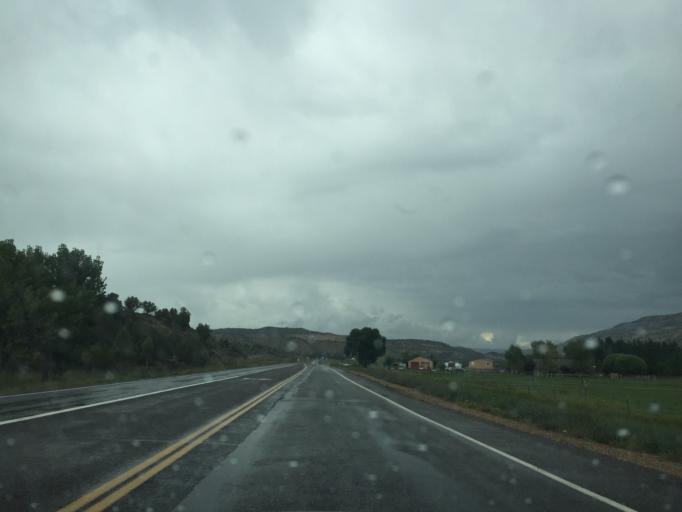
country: US
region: Utah
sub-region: Kane County
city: Kanab
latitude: 37.2594
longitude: -112.6573
